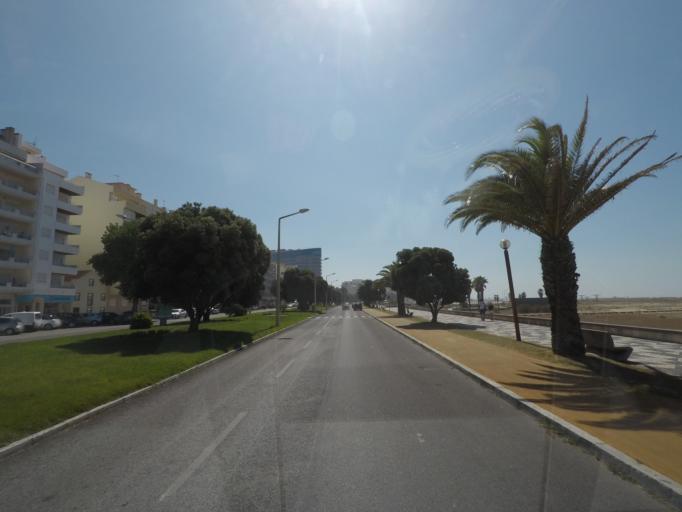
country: PT
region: Coimbra
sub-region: Figueira da Foz
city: Buarcos
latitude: 40.1585
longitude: -8.8695
